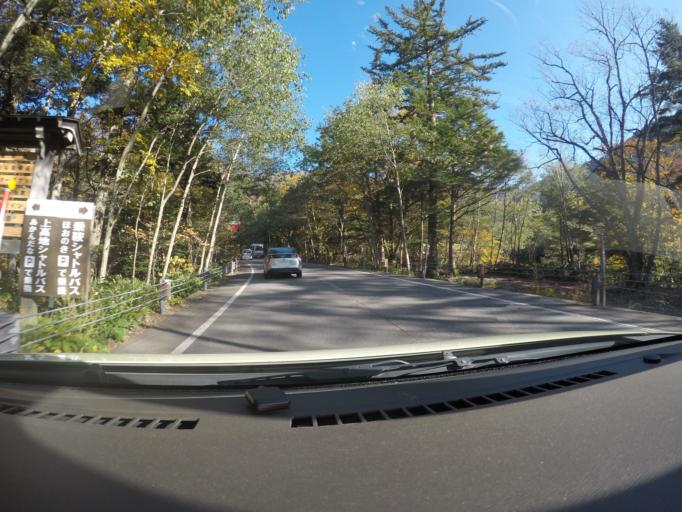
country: JP
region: Gifu
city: Takayama
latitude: 36.1861
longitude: 137.5499
